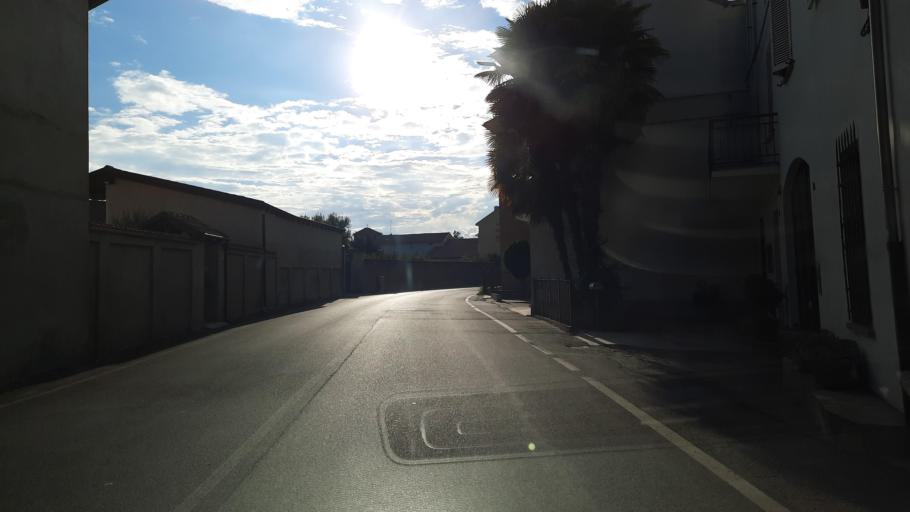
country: IT
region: Piedmont
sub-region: Provincia di Vercelli
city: Trino
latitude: 45.1991
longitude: 8.2955
